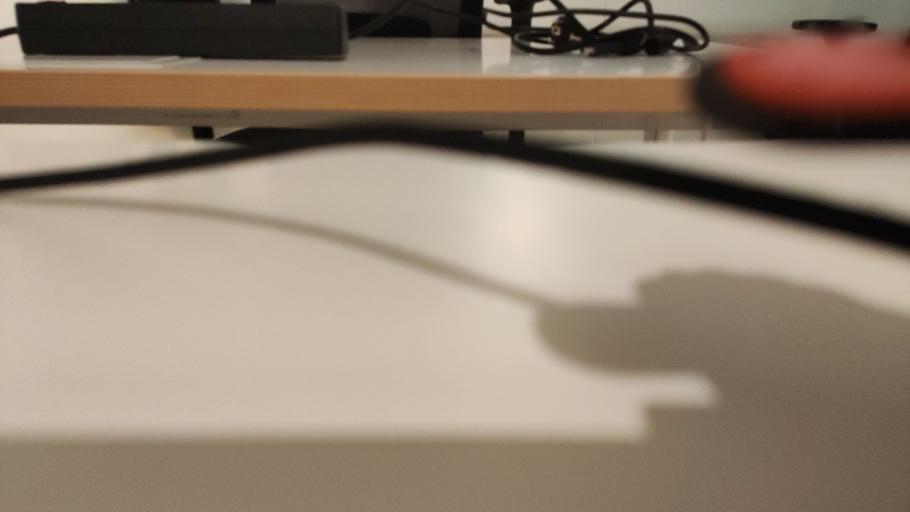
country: RU
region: Moskovskaya
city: Proletarskiy
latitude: 54.9840
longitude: 37.3282
